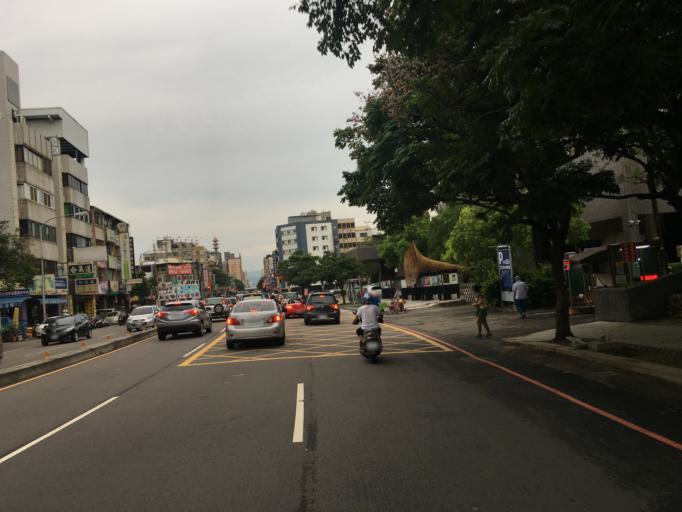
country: TW
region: Taiwan
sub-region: Taichung City
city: Taichung
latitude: 24.1421
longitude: 120.6655
